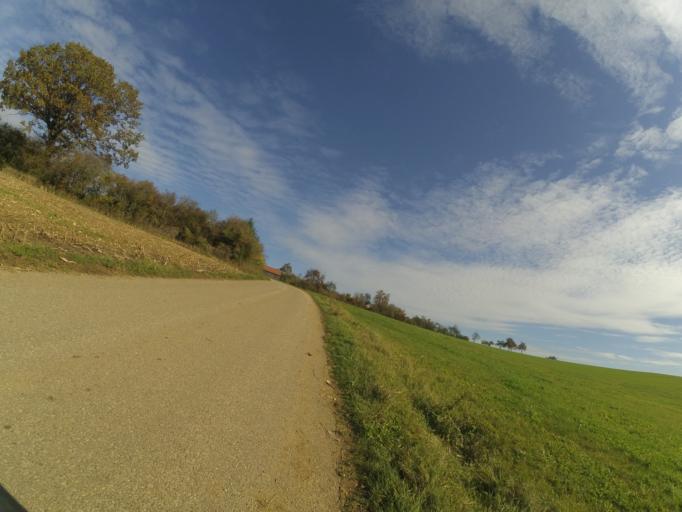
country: DE
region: Baden-Wuerttemberg
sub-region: Tuebingen Region
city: Weidenstetten
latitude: 48.5870
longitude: 9.9851
